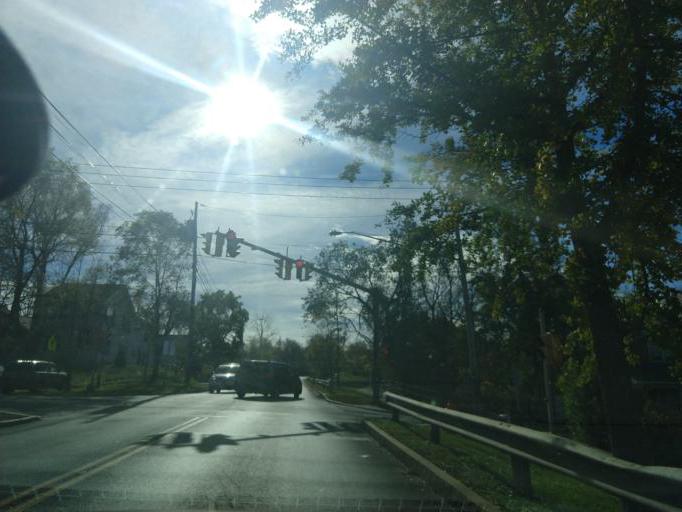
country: US
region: New York
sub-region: Tompkins County
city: South Hill
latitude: 42.4351
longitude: -76.4946
